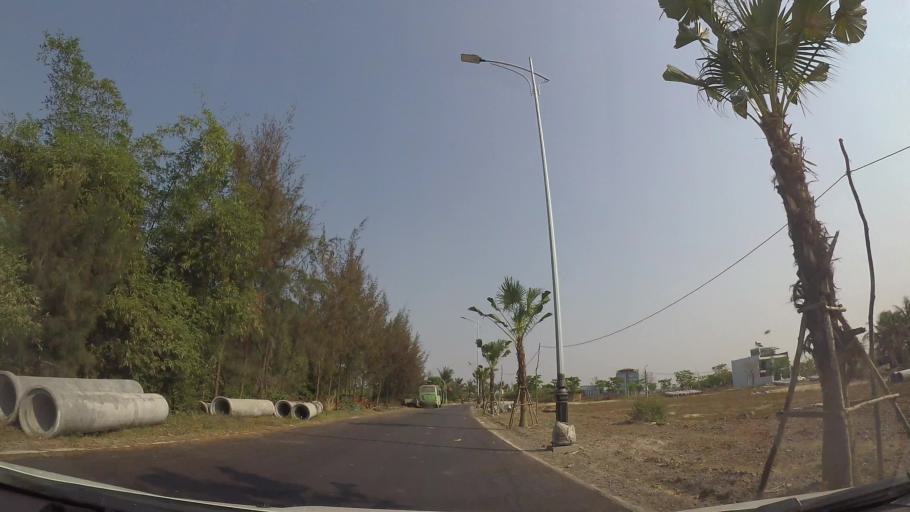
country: VN
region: Da Nang
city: Ngu Hanh Son
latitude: 15.9584
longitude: 108.2818
